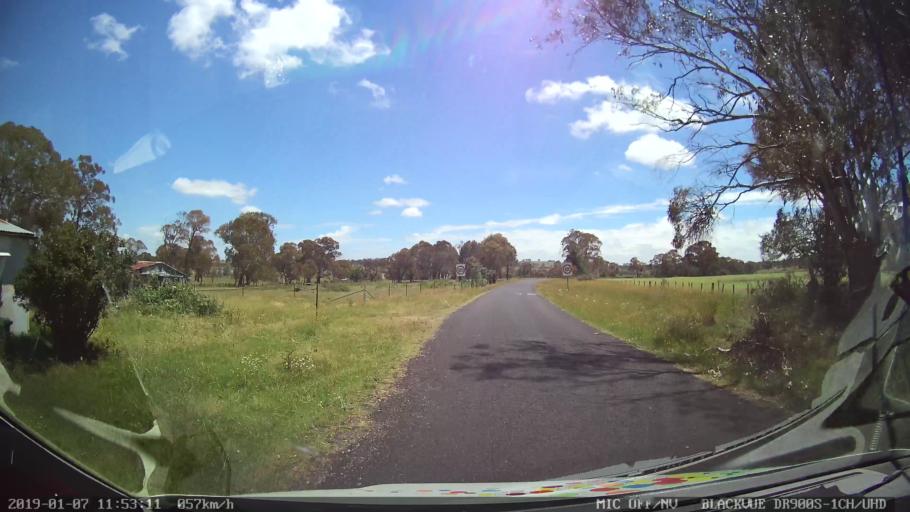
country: AU
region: New South Wales
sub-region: Guyra
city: Guyra
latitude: -30.3063
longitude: 151.6561
